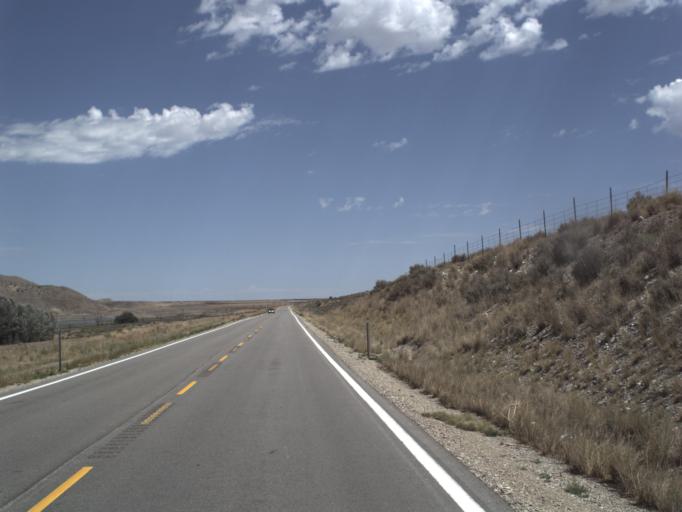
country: US
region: Utah
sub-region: Tooele County
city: Tooele
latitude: 40.4159
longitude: -112.3830
